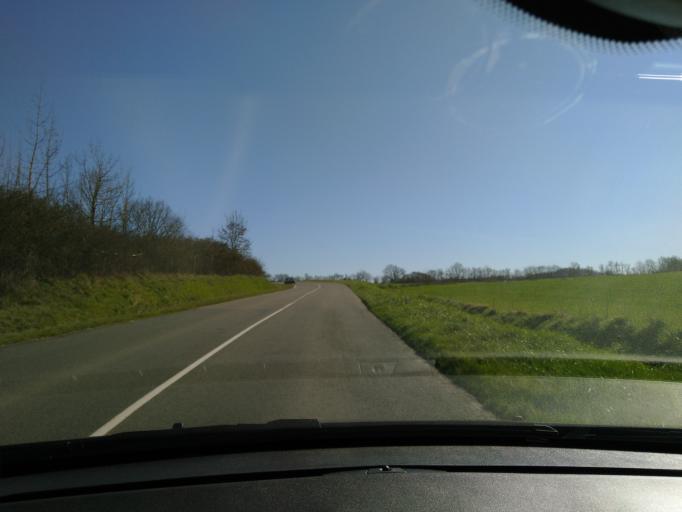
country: FR
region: Aquitaine
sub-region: Departement du Lot-et-Garonne
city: Cancon
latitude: 44.5371
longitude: 0.6699
